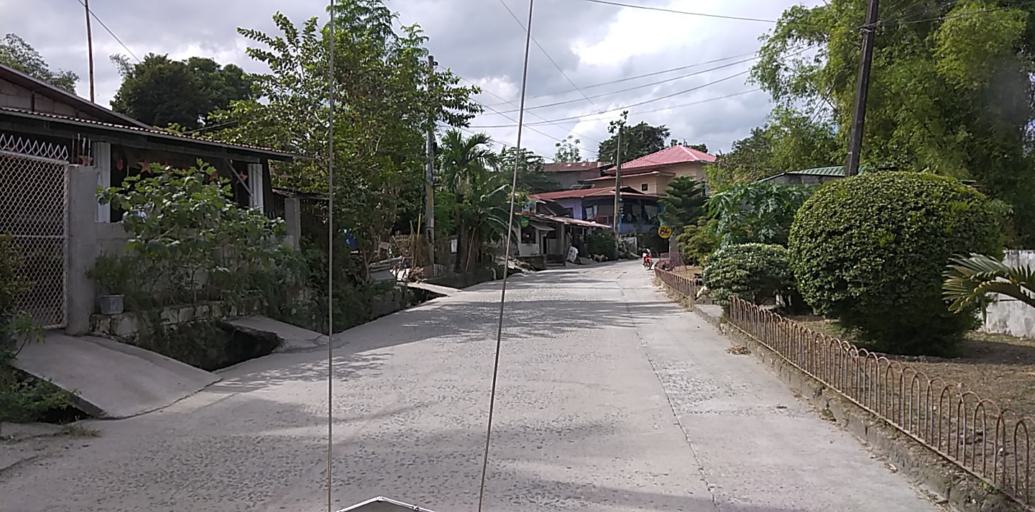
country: PH
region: Central Luzon
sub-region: Province of Pampanga
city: Porac
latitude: 15.0660
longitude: 120.5387
